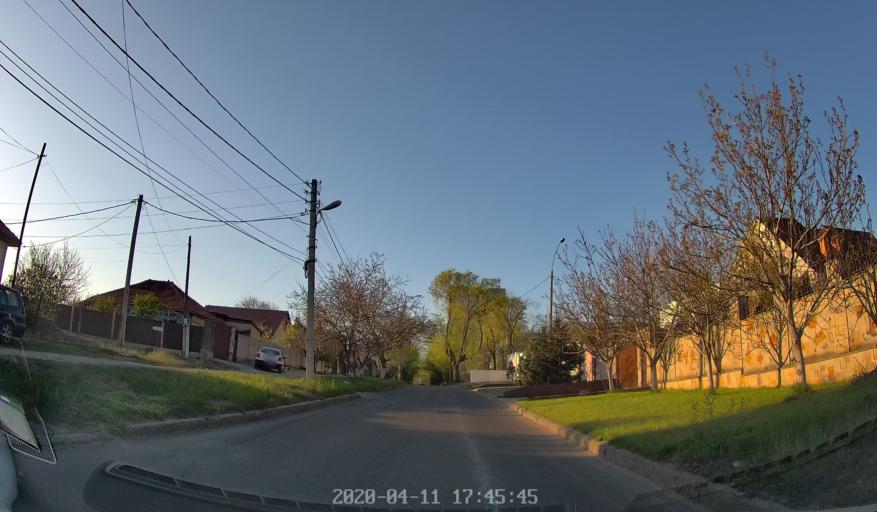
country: MD
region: Chisinau
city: Chisinau
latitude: 46.9876
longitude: 28.8220
